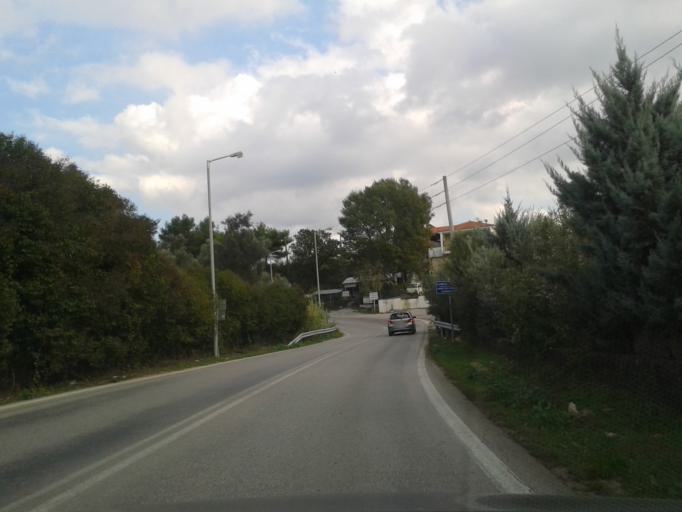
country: GR
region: Attica
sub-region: Nomarchia Anatolikis Attikis
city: Polydendri
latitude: 38.2070
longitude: 23.8677
